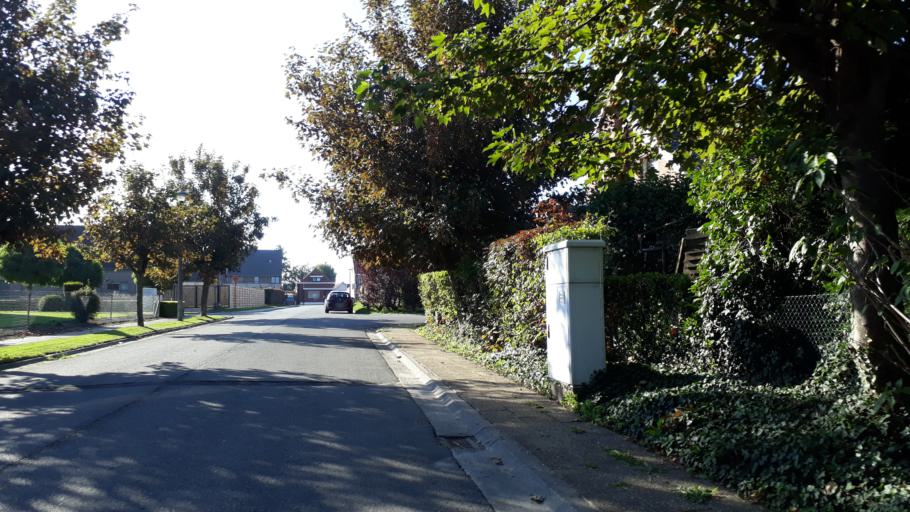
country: BE
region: Flanders
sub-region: Provincie West-Vlaanderen
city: Torhout
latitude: 51.0655
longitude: 3.1169
